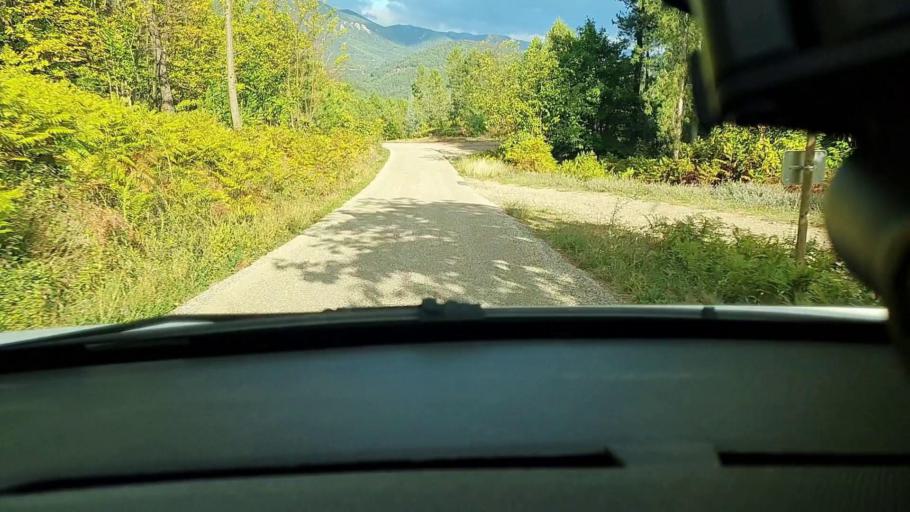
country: FR
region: Languedoc-Roussillon
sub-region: Departement du Gard
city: Besseges
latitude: 44.3444
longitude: 3.9854
